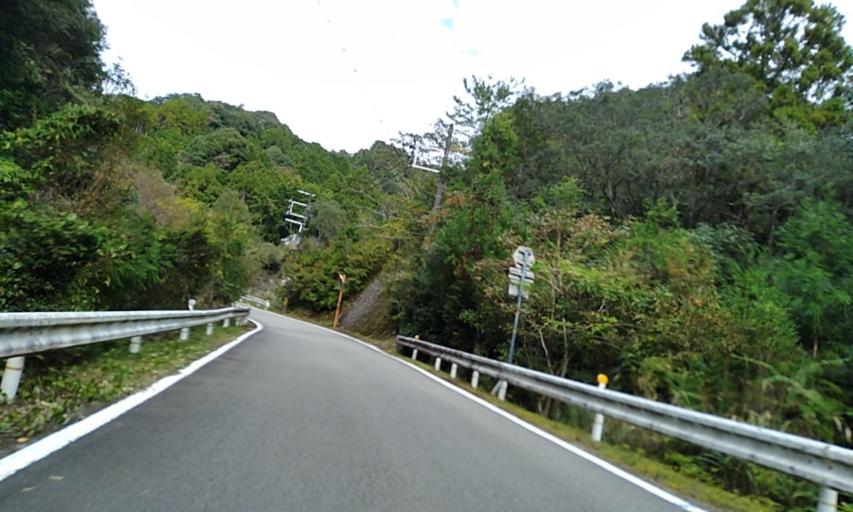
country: JP
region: Wakayama
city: Shingu
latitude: 33.5427
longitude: 135.8452
